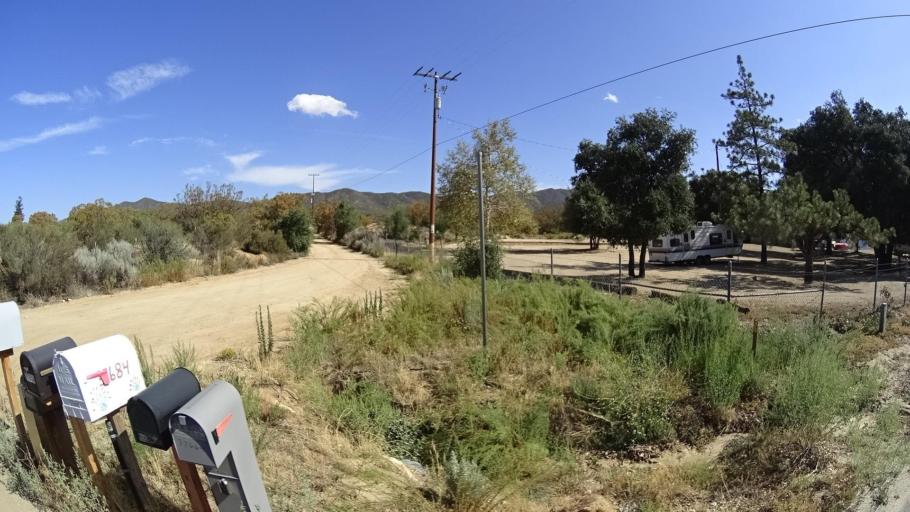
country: US
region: California
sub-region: Riverside County
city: Anza
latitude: 33.3852
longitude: -116.6608
